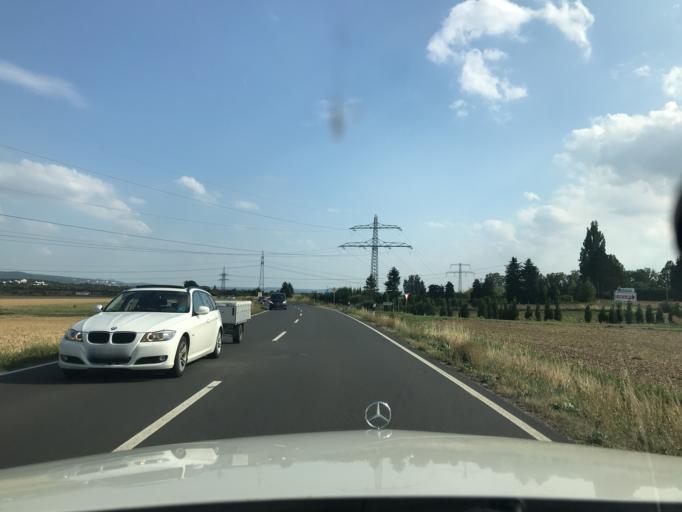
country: DE
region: Lower Saxony
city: Bovenden
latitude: 51.5731
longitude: 9.8780
